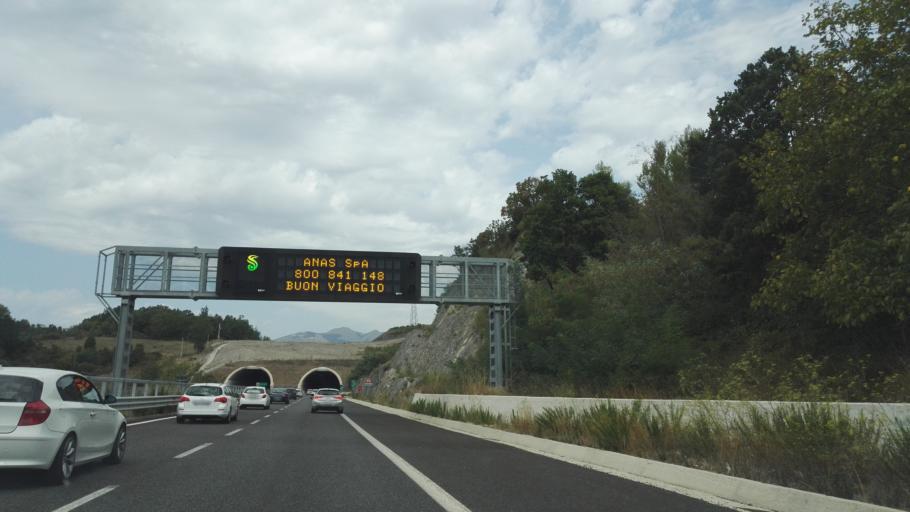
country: IT
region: Basilicate
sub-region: Provincia di Potenza
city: Lauria
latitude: 40.0264
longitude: 15.8772
